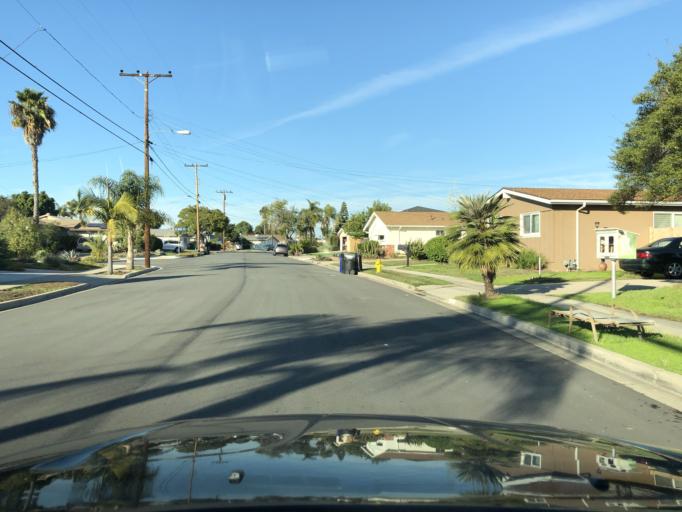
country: US
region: California
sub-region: San Diego County
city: La Jolla
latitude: 32.8201
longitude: -117.1957
